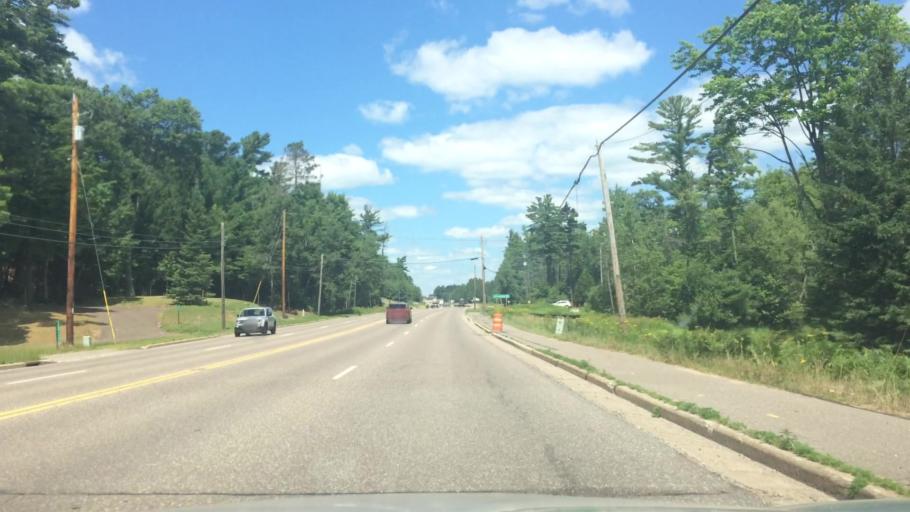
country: US
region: Wisconsin
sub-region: Vilas County
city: Lac du Flambeau
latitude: 45.9087
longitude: -89.6946
